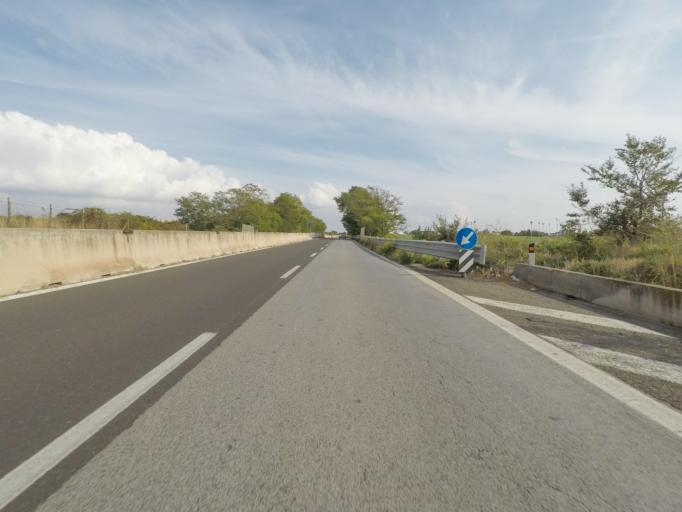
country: IT
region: Latium
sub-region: Provincia di Viterbo
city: Montalto di Castro
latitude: 42.3468
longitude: 11.6079
